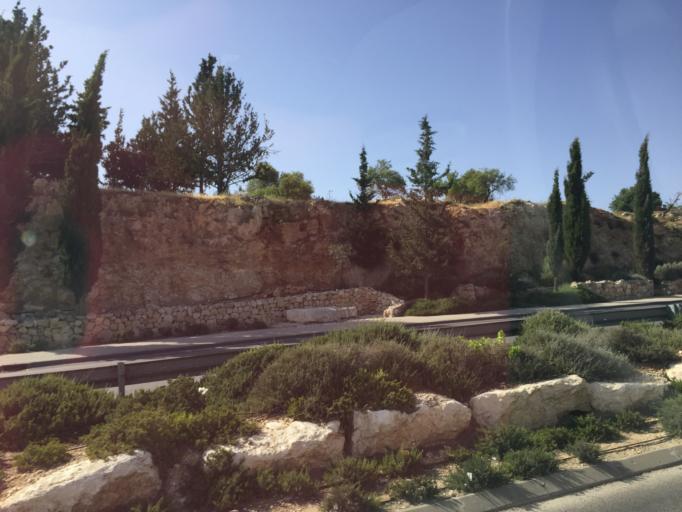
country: PS
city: Khallat Hamamah
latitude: 31.7328
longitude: 35.2077
